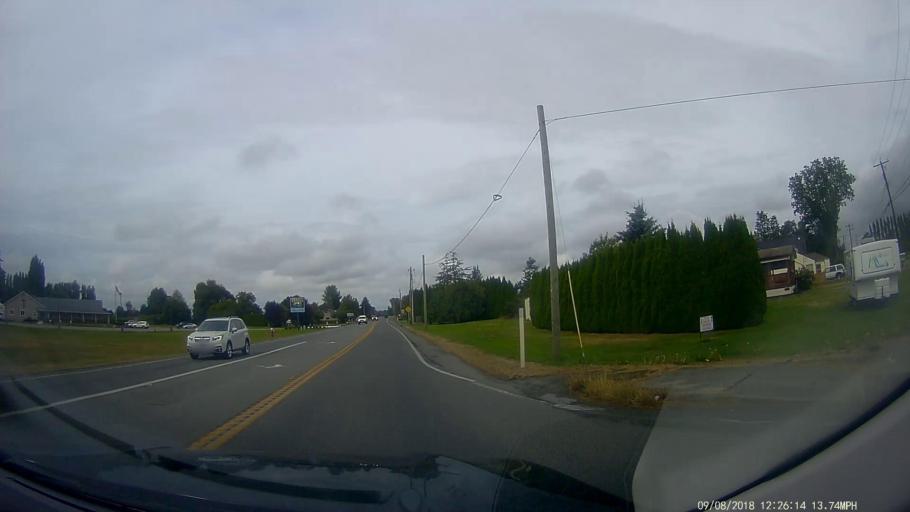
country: US
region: Washington
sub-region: Skagit County
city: Mount Vernon
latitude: 48.4362
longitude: -122.3782
